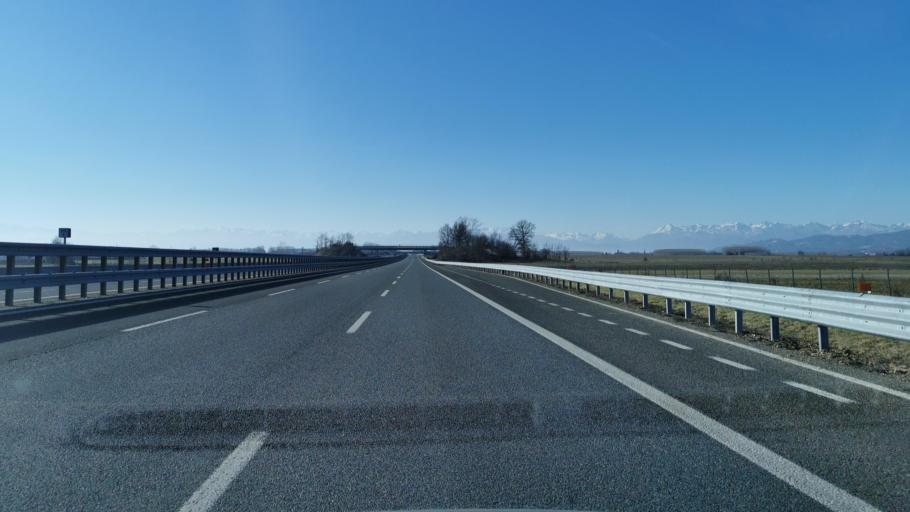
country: IT
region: Piedmont
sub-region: Provincia di Torino
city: Pessione
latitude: 44.9578
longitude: 7.8336
